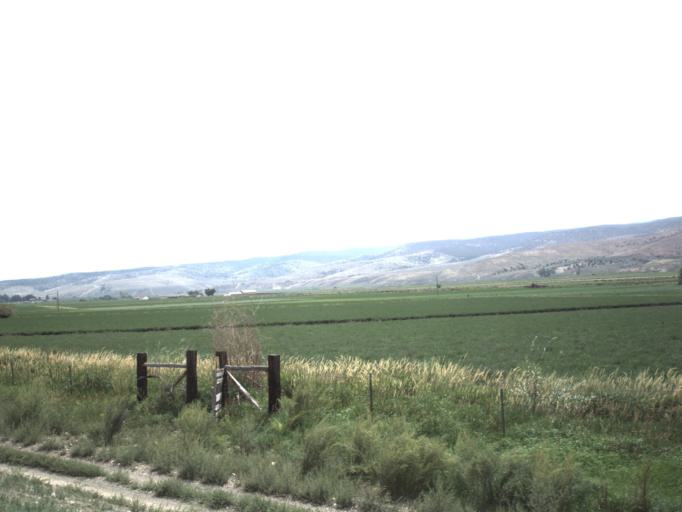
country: US
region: Utah
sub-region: Piute County
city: Junction
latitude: 38.1499
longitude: -112.0007
